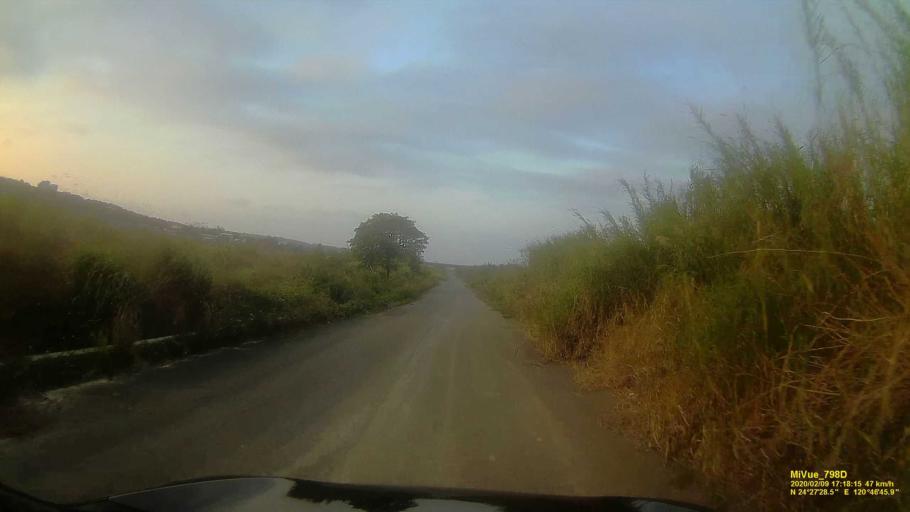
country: TW
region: Taiwan
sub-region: Miaoli
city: Miaoli
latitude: 24.4580
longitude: 120.7794
